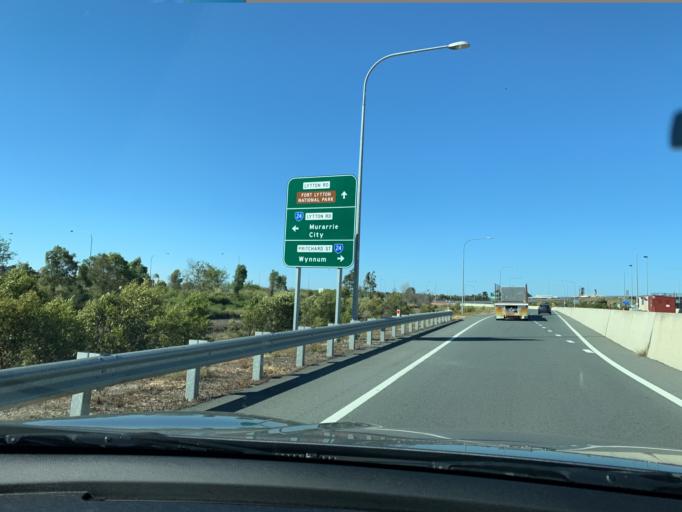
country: AU
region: Queensland
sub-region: Brisbane
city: Wynnum
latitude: -27.4280
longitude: 153.1442
